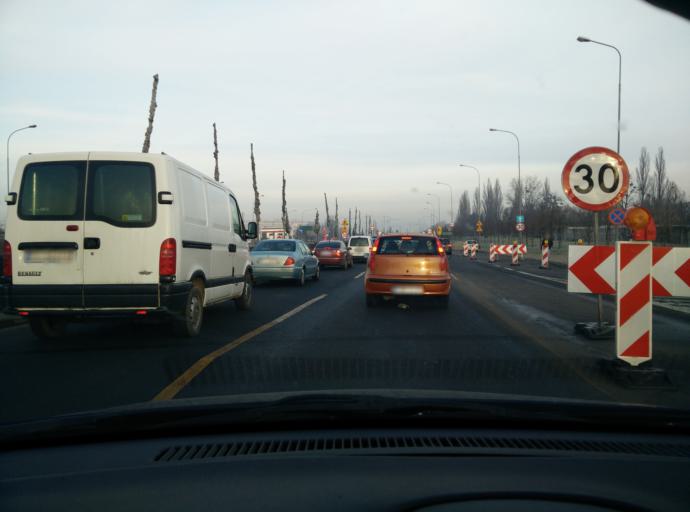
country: PL
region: Greater Poland Voivodeship
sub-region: Poznan
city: Poznan
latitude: 52.3862
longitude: 16.9703
